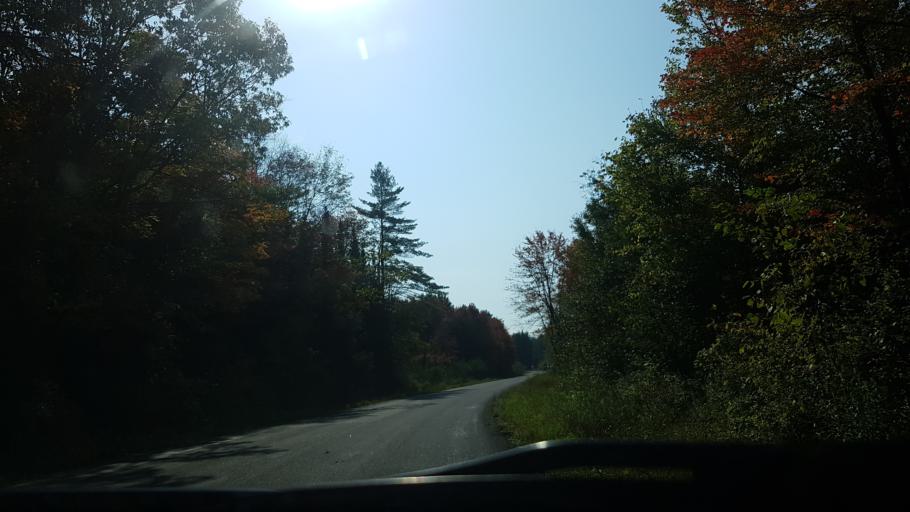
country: CA
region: Ontario
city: Bracebridge
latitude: 44.9707
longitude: -79.2571
